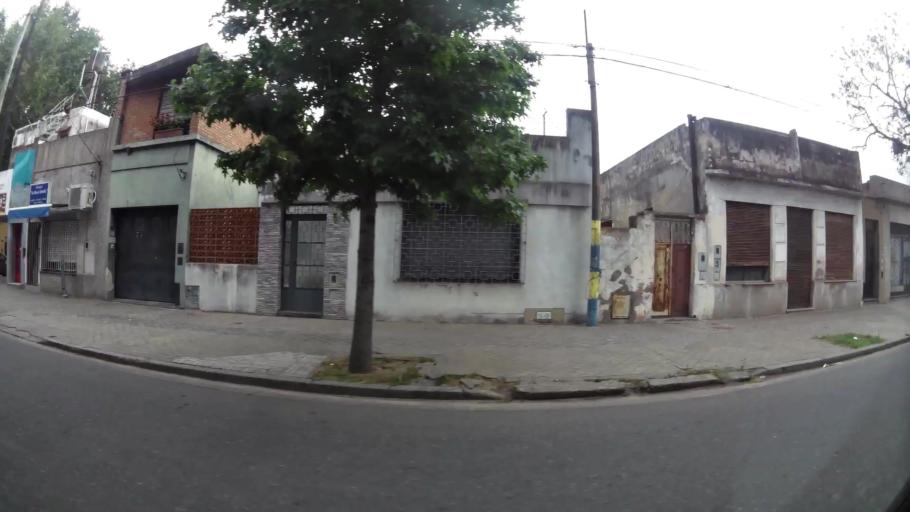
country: AR
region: Santa Fe
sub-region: Departamento de Rosario
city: Rosario
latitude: -32.9150
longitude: -60.6769
